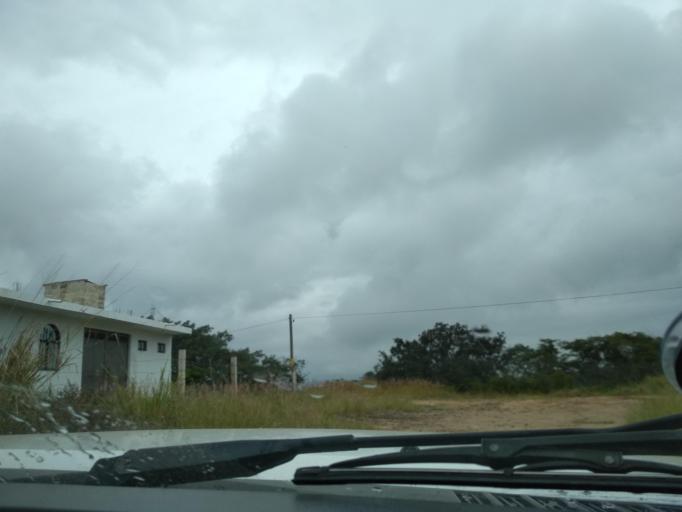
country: MX
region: Veracruz
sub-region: Emiliano Zapata
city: Dos Rios
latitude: 19.5341
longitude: -96.8131
